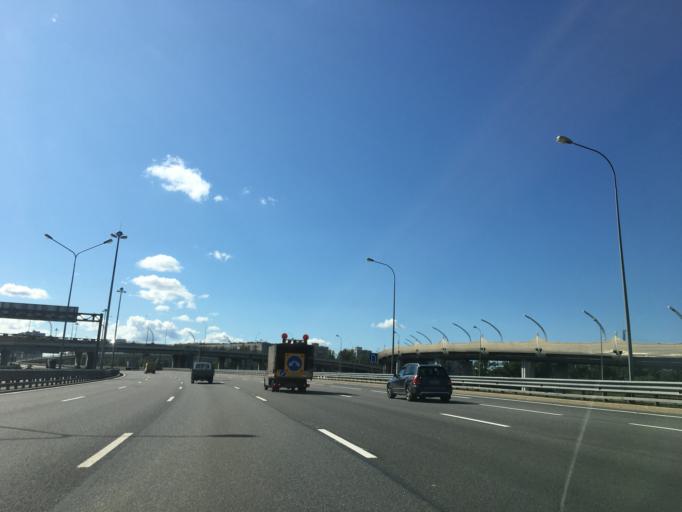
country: RU
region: St.-Petersburg
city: Dachnoye
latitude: 59.8348
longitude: 30.2740
